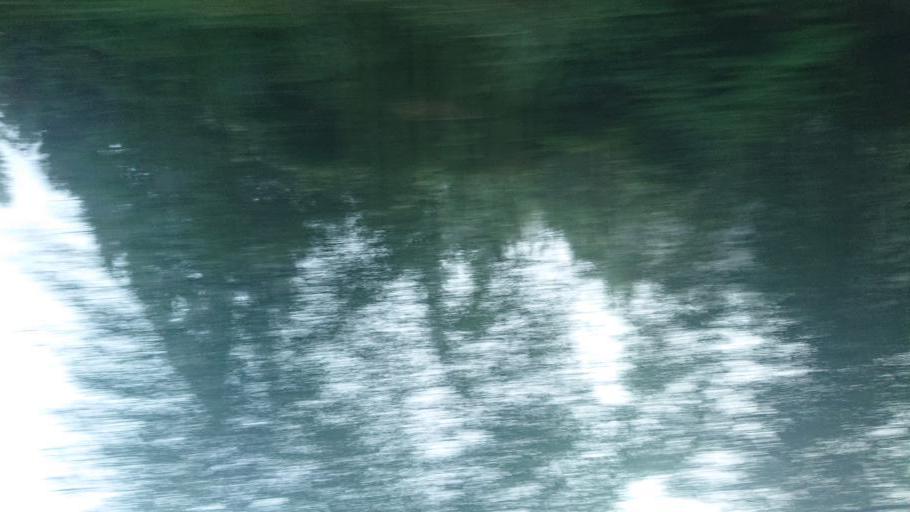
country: TW
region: Taiwan
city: Lugu
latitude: 23.5103
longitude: 120.7010
